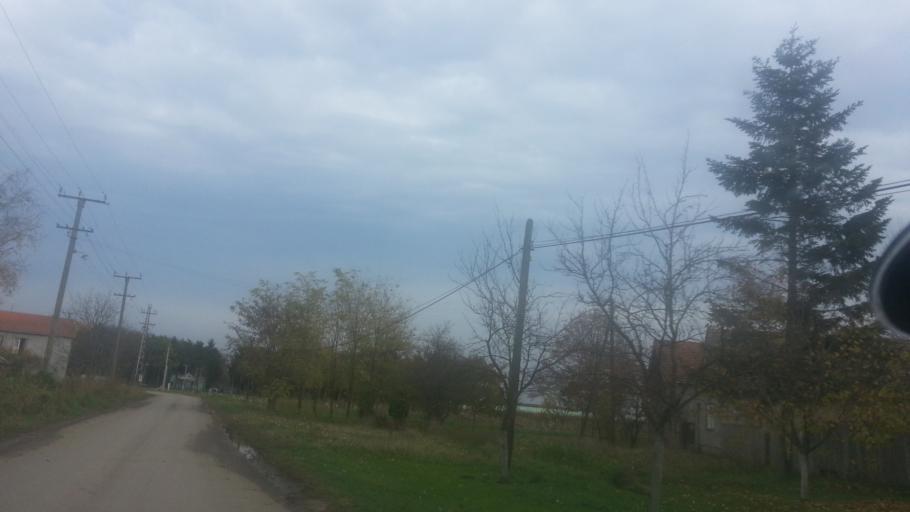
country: RS
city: Putinci
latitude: 44.9960
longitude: 19.9760
